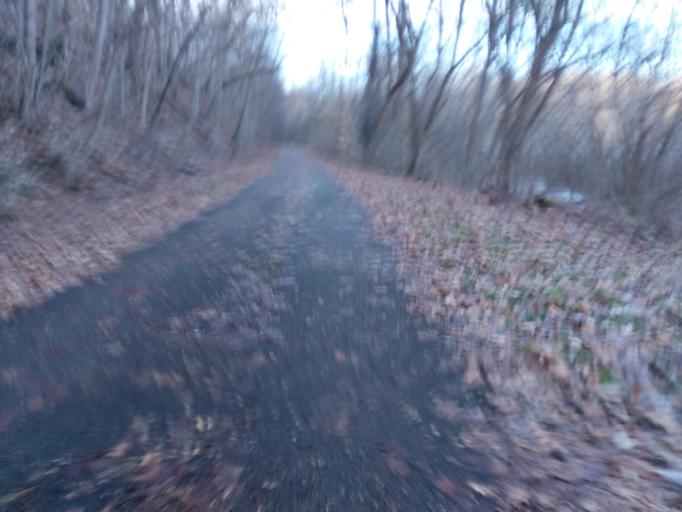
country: US
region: Ohio
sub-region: Athens County
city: Athens
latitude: 39.3502
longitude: -82.1026
